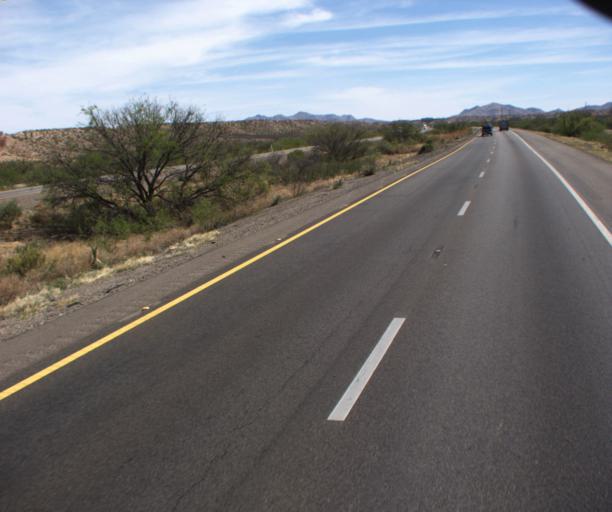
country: US
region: Arizona
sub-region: Cochise County
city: Benson
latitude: 31.9689
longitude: -110.2432
